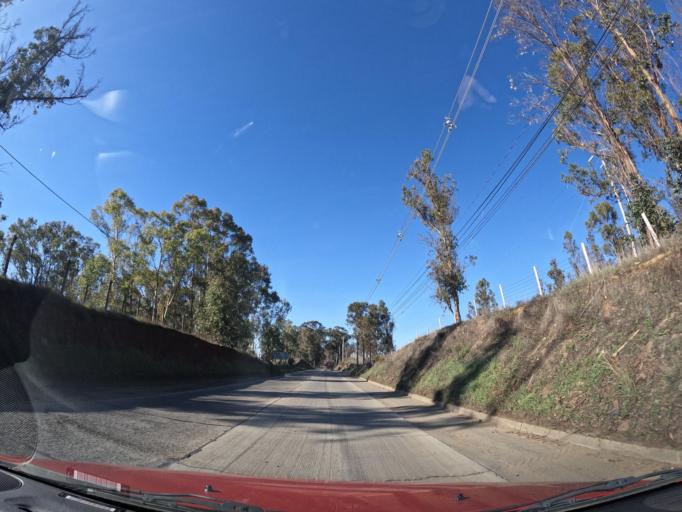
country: CL
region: Maule
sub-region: Provincia de Cauquenes
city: Cauquenes
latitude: -35.9579
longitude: -72.2933
